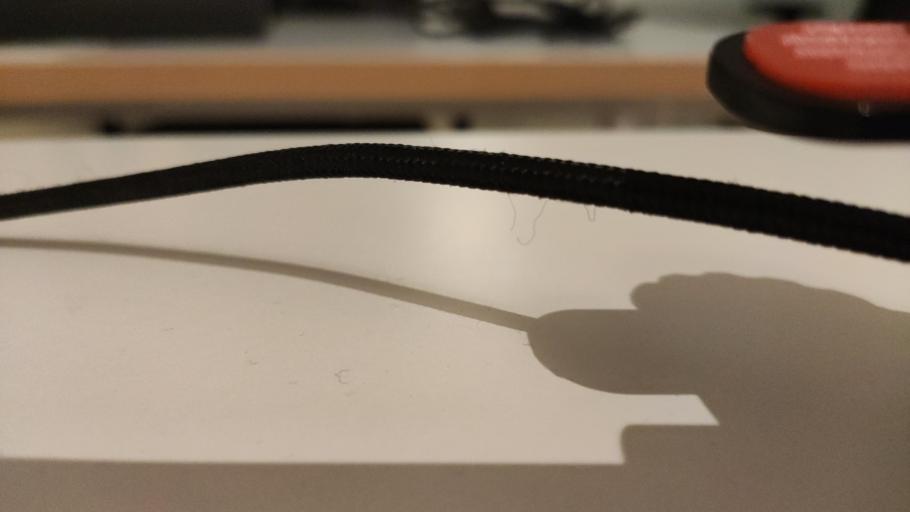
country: RU
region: Moskovskaya
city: Malaya Dubna
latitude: 55.8580
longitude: 38.9623
